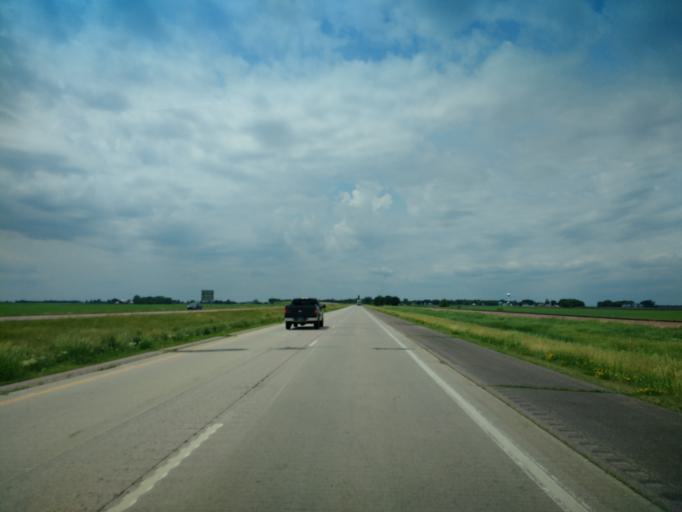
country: US
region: Minnesota
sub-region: Watonwan County
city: Saint James
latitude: 43.9621
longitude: -94.7613
